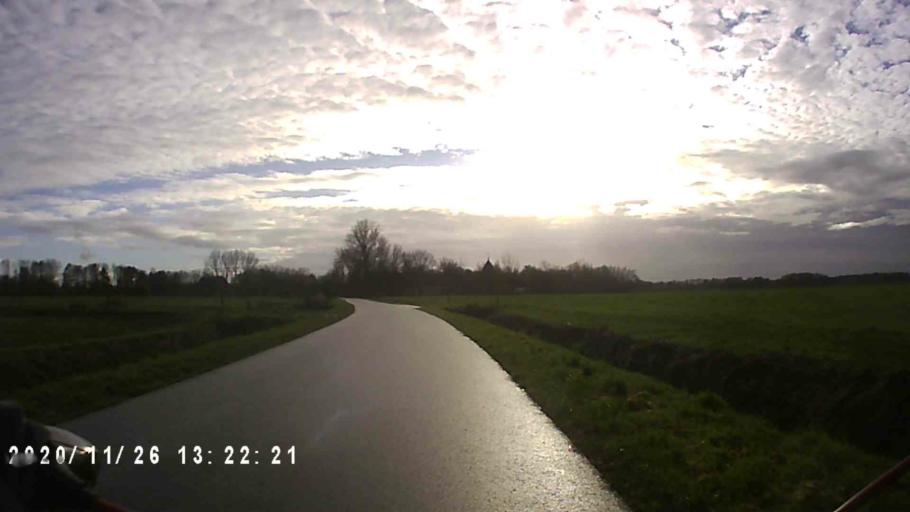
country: NL
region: Groningen
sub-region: Gemeente Delfzijl
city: Delfzijl
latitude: 53.3458
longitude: 6.8934
